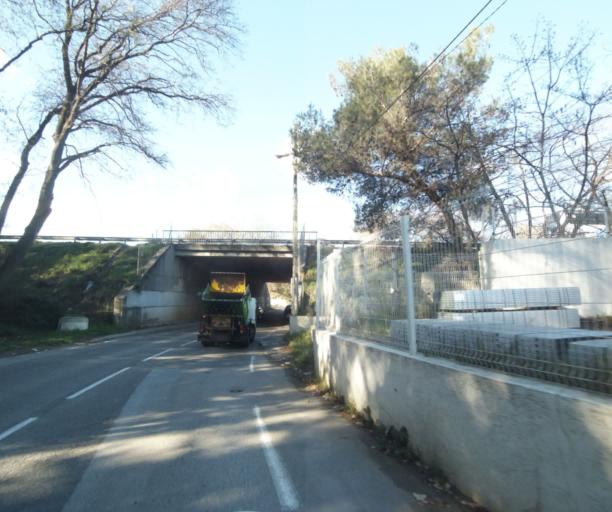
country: FR
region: Provence-Alpes-Cote d'Azur
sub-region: Departement des Alpes-Maritimes
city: Biot
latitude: 43.6114
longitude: 7.1090
